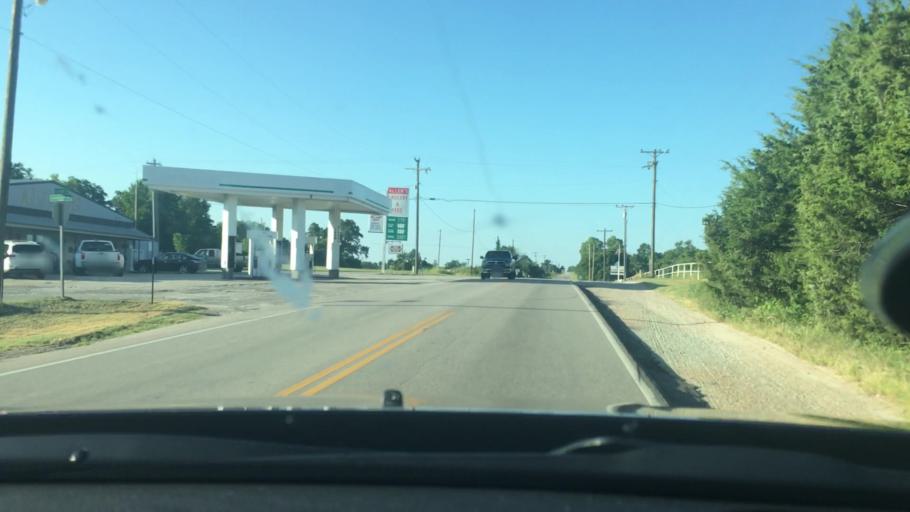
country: US
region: Oklahoma
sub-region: Murray County
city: Sulphur
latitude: 34.6212
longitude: -96.8447
